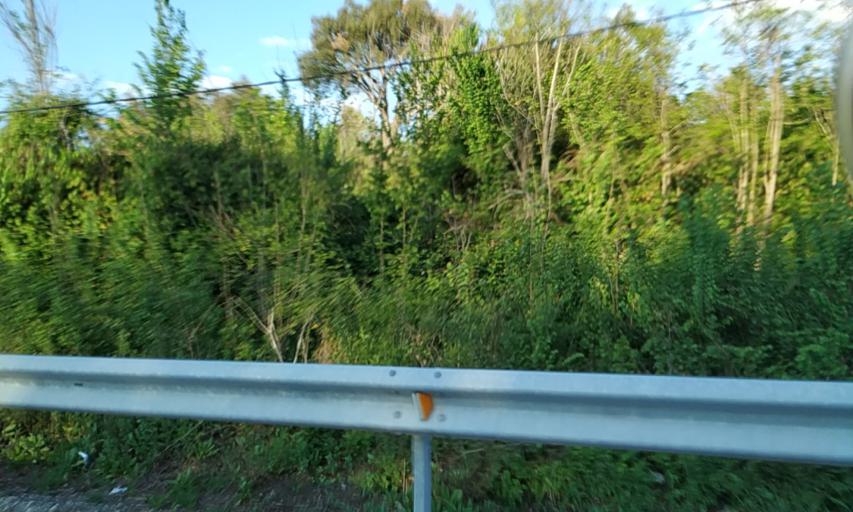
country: PT
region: Portalegre
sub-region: Portalegre
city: Sao Juliao
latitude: 39.3480
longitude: -7.2753
